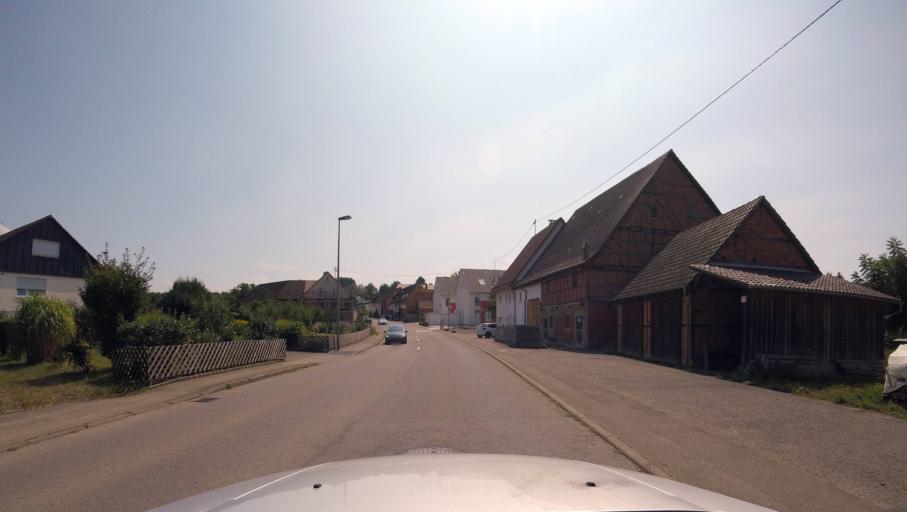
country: DE
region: Baden-Wuerttemberg
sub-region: Regierungsbezirk Stuttgart
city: Oppenweiler
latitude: 48.9560
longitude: 9.4786
